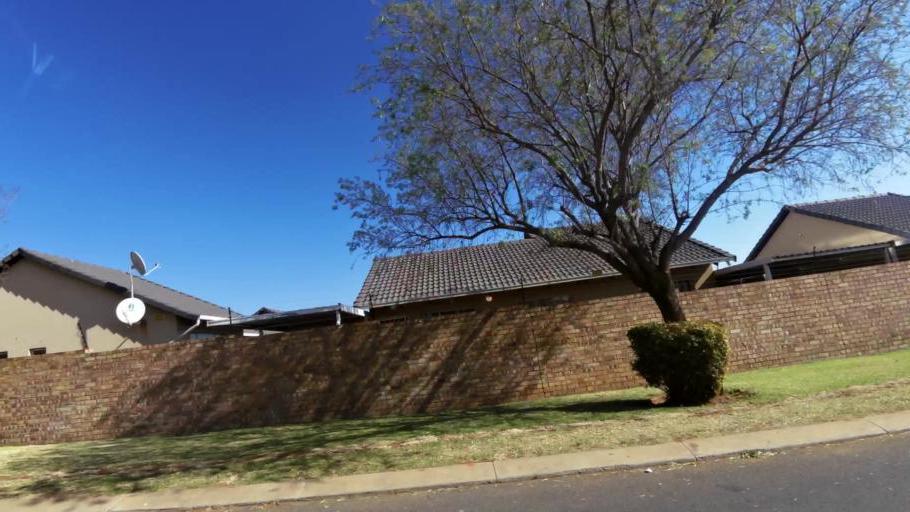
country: ZA
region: Gauteng
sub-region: City of Johannesburg Metropolitan Municipality
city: Johannesburg
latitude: -26.2424
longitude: 27.9997
